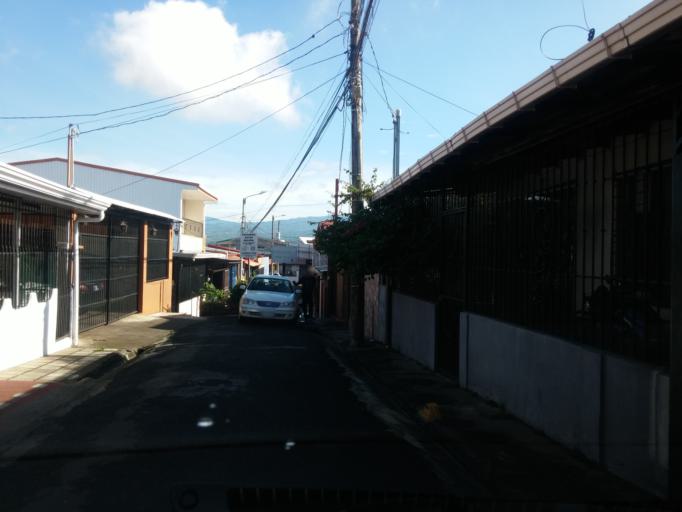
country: CR
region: Heredia
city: Mercedes
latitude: 10.0029
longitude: -84.1399
